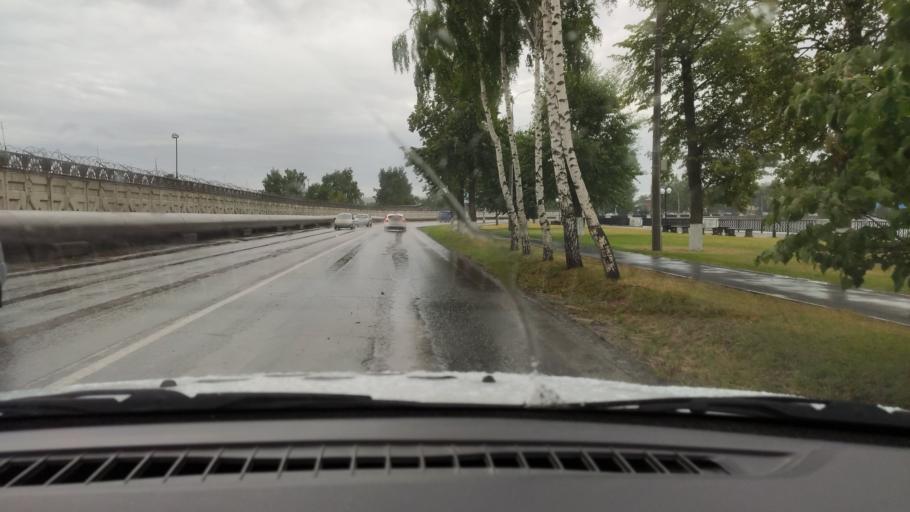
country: RU
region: Udmurtiya
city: Votkinsk
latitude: 57.0514
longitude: 53.9774
